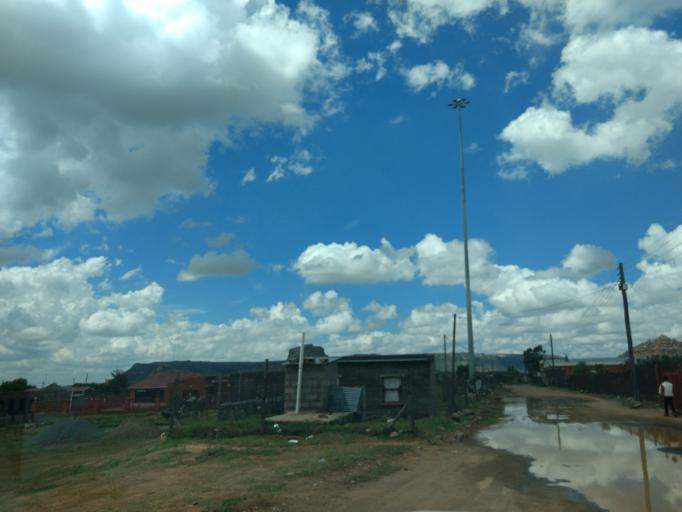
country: LS
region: Maseru
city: Maseru
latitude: -29.3679
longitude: 27.5133
